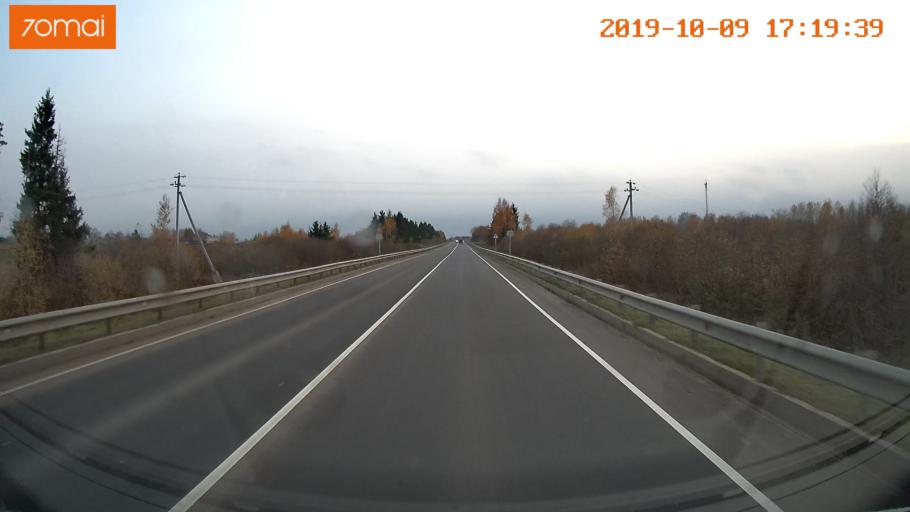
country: RU
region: Ivanovo
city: Furmanov
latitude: 57.2435
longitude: 41.1503
